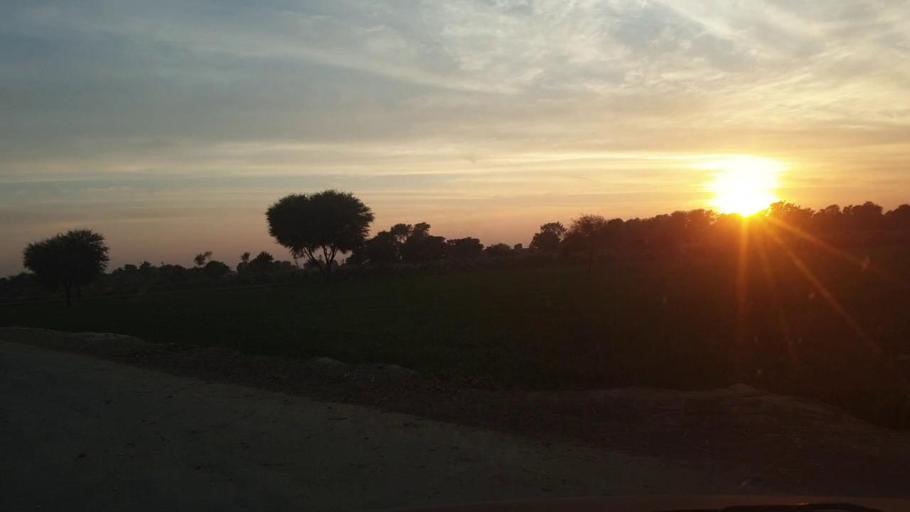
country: PK
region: Sindh
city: Shahpur Chakar
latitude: 26.0747
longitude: 68.5248
